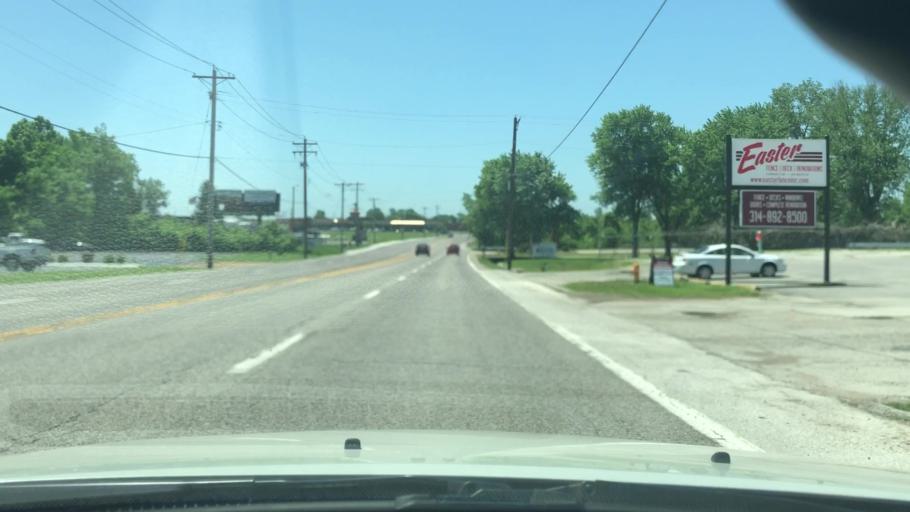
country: US
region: Missouri
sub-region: Jefferson County
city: Arnold
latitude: 38.4680
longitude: -90.3560
